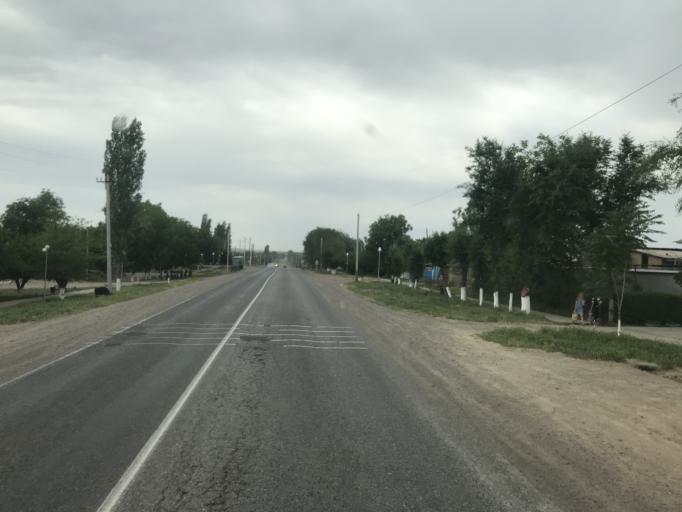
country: UZ
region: Toshkent
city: Salor
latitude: 41.4938
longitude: 69.3161
